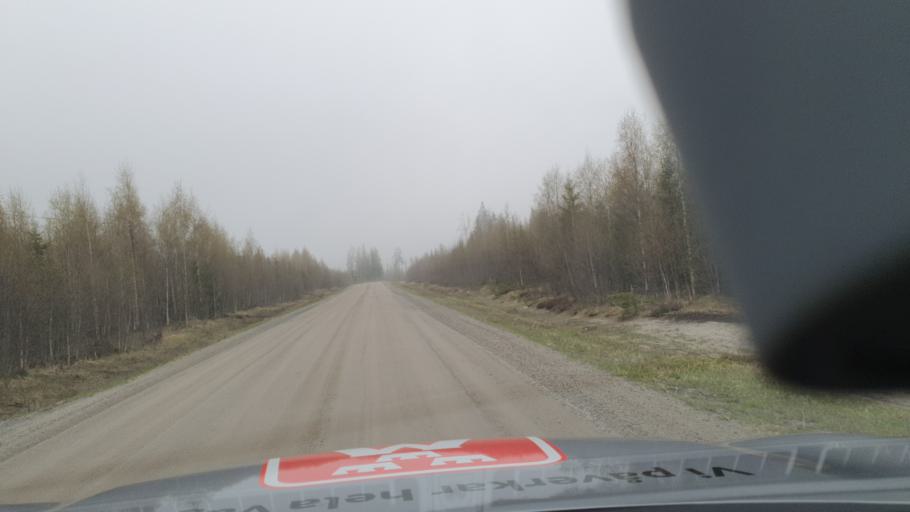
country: SE
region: Vaesternorrland
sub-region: OErnskoeldsviks Kommun
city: Husum
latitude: 63.6041
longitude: 19.0247
